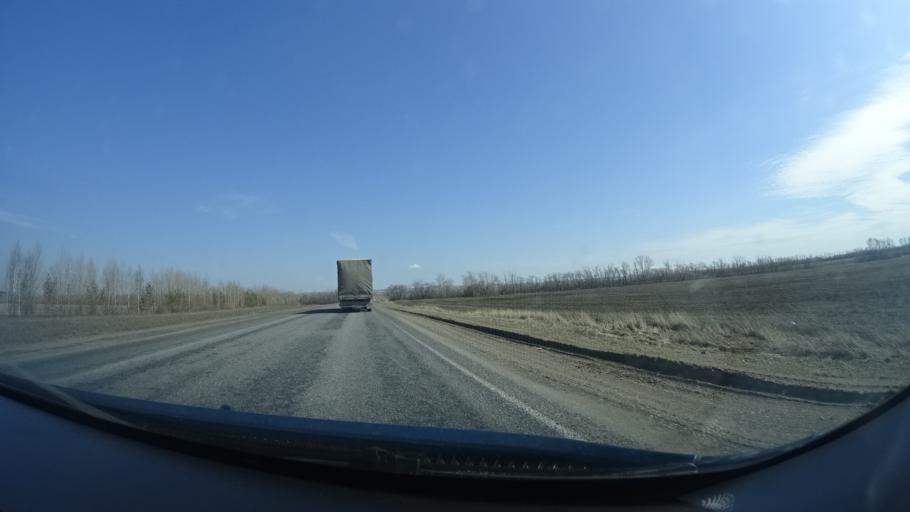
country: RU
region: Bashkortostan
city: Subkhankulovo
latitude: 54.4850
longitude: 53.8779
